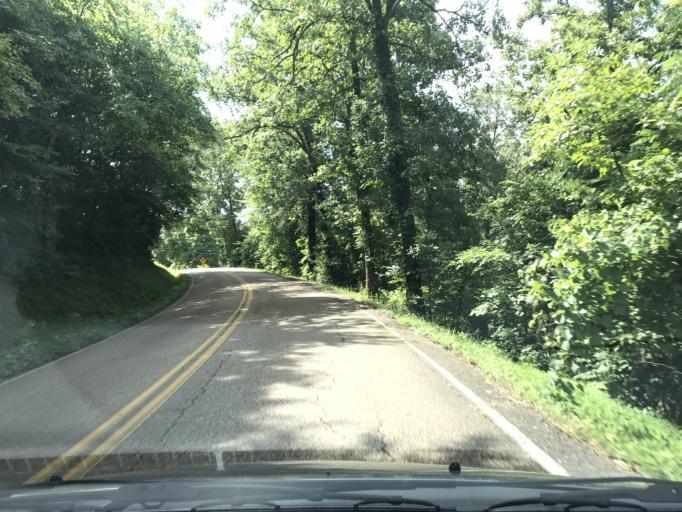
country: US
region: Tennessee
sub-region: Hamilton County
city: Lakesite
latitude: 35.1761
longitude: -85.0628
